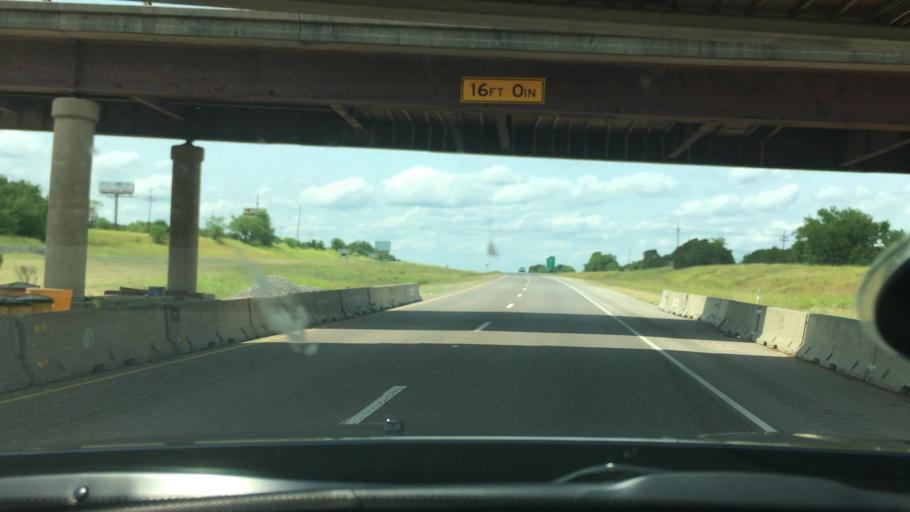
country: US
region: Oklahoma
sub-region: Murray County
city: Davis
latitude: 34.4880
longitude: -97.1610
